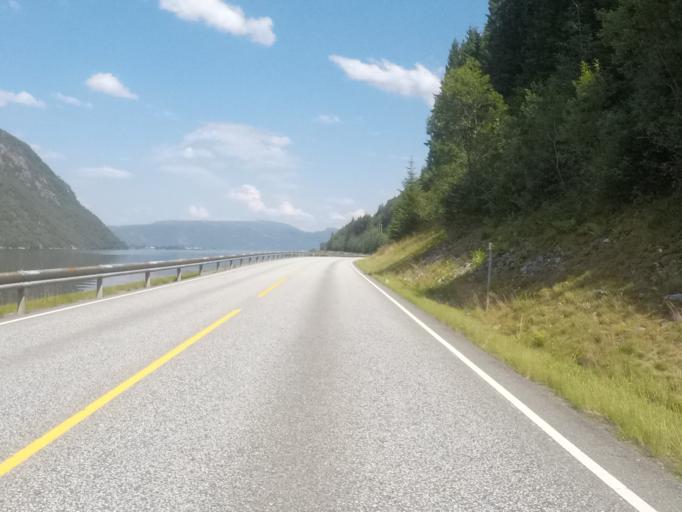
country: NO
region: Sogn og Fjordane
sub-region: Hyllestad
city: Hyllestad
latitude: 60.9899
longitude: 5.4863
